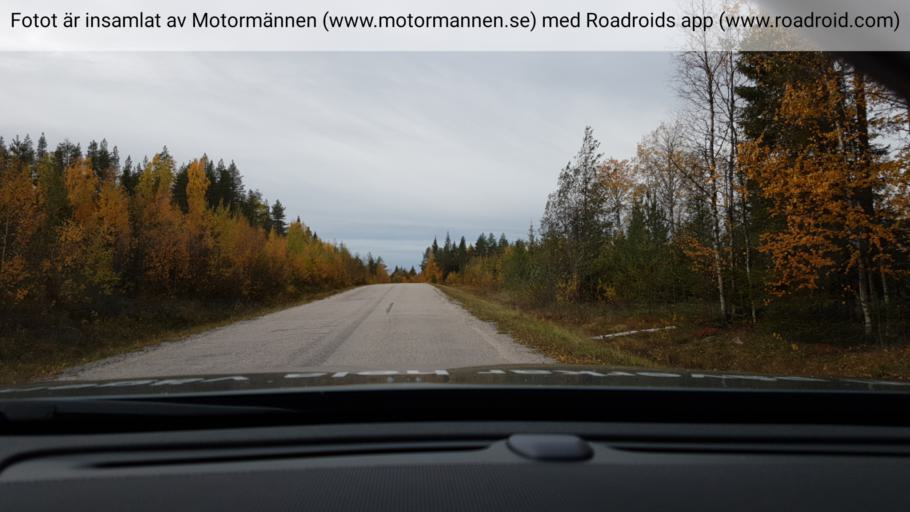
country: SE
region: Norrbotten
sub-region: Overkalix Kommun
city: OEverkalix
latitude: 66.2579
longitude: 23.0802
